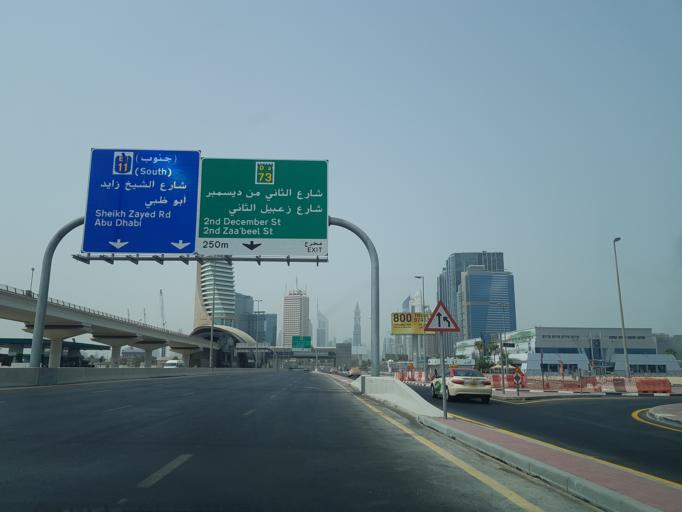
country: AE
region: Ash Shariqah
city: Sharjah
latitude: 25.2360
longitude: 55.2930
